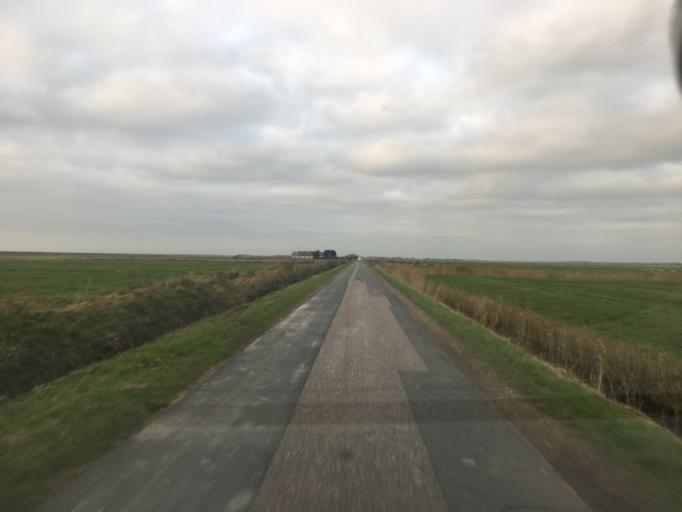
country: DE
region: Schleswig-Holstein
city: Klanxbull
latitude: 54.9272
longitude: 8.6795
